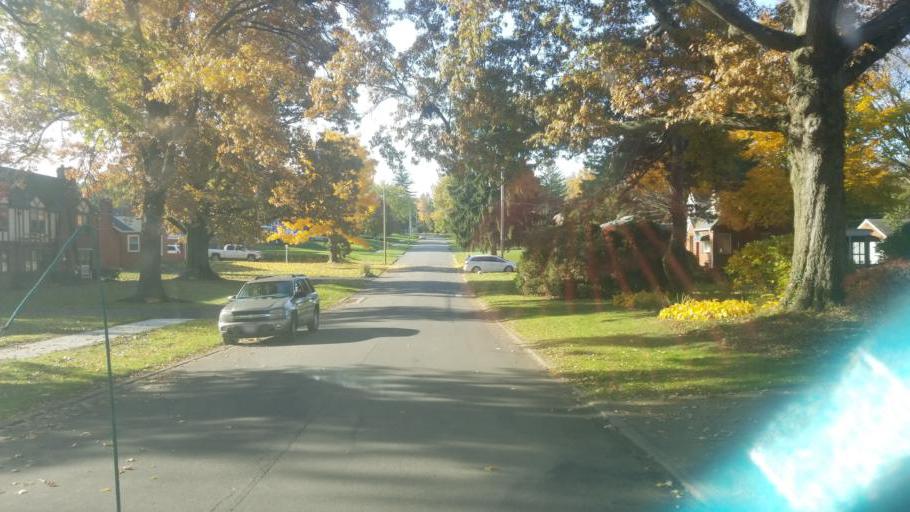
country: US
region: Ohio
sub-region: Richland County
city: Mansfield
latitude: 40.7414
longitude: -82.5287
